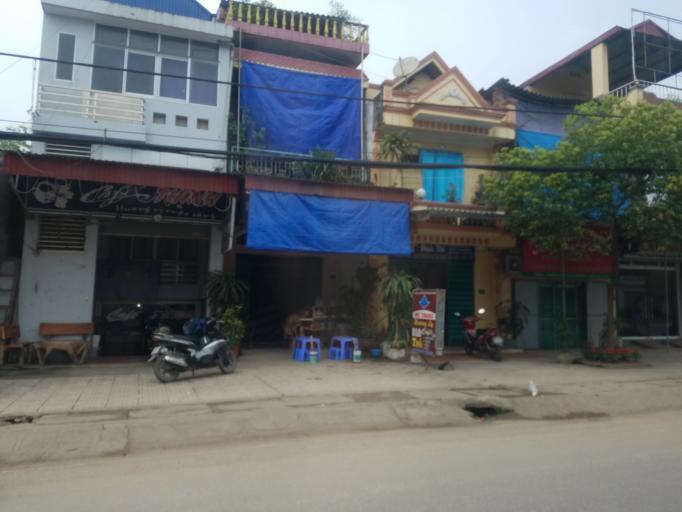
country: VN
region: Thai Nguyen
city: Chua Hang
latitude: 21.6148
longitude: 105.8393
